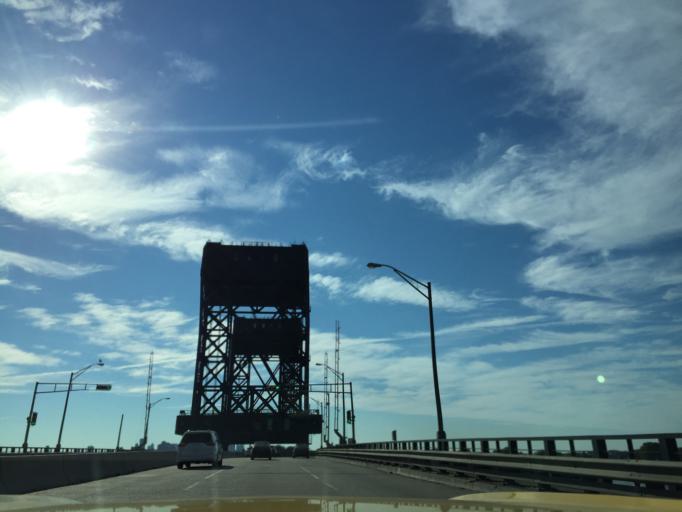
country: US
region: New Jersey
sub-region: Hudson County
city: Jersey City
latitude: 40.7280
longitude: -74.1012
